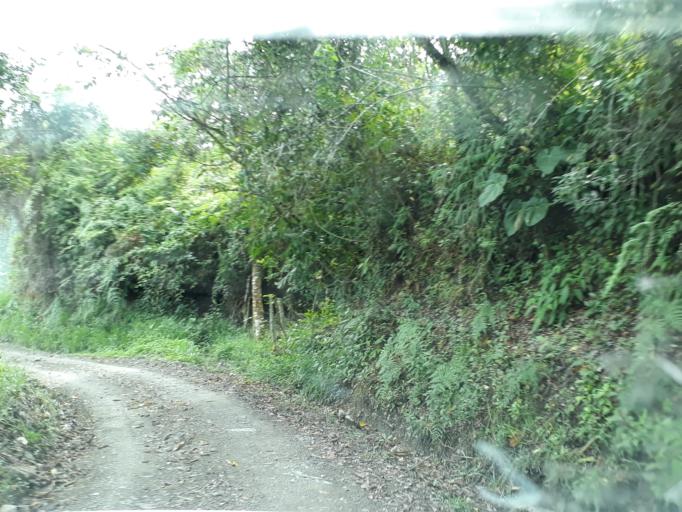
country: CO
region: Cundinamarca
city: Pacho
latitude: 5.1737
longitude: -74.2477
